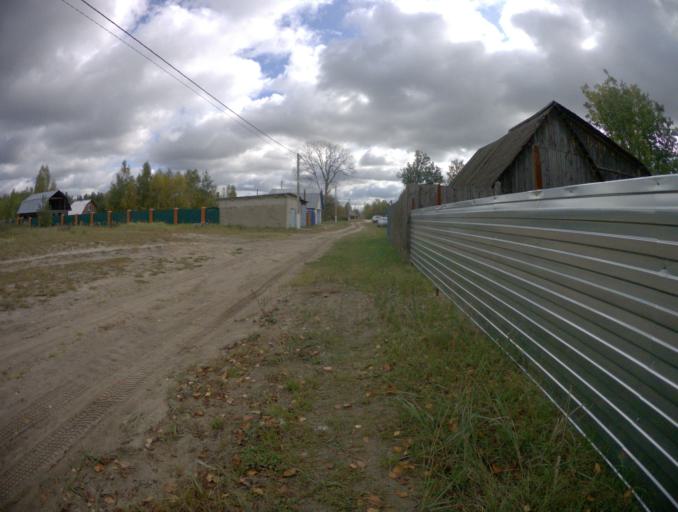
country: RU
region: Moskovskaya
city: Baksheyevo
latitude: 55.7157
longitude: 39.8586
